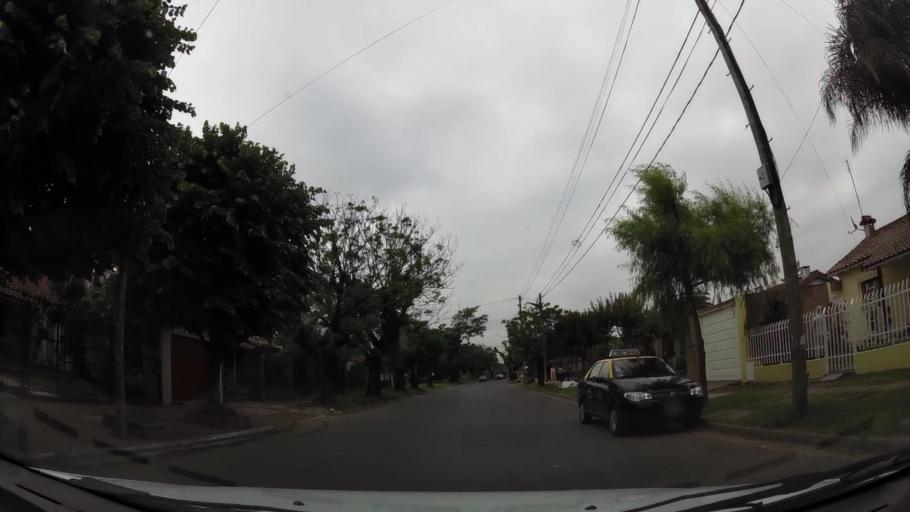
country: AR
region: Buenos Aires
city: San Justo
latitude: -34.7095
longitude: -58.5424
